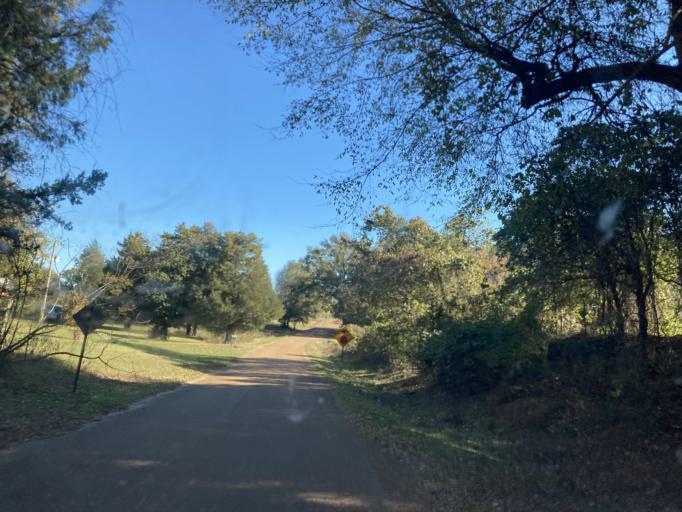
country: US
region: Mississippi
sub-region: Madison County
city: Kearney Park
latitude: 32.7161
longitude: -90.3759
